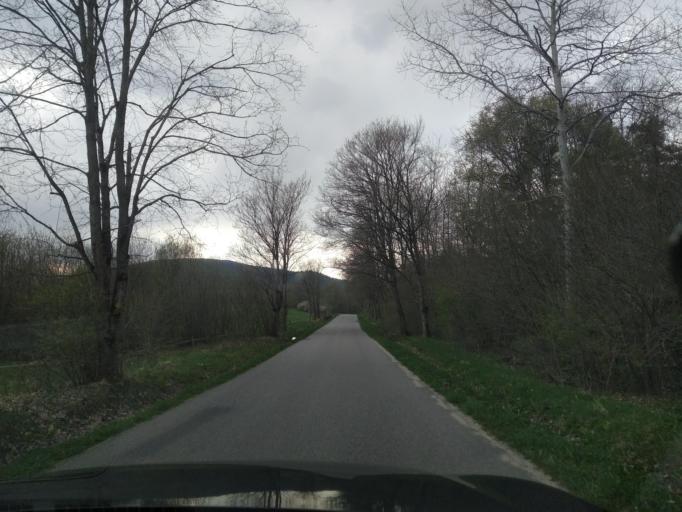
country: PL
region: Subcarpathian Voivodeship
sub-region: Powiat leski
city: Baligrod
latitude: 49.3577
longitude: 22.2171
